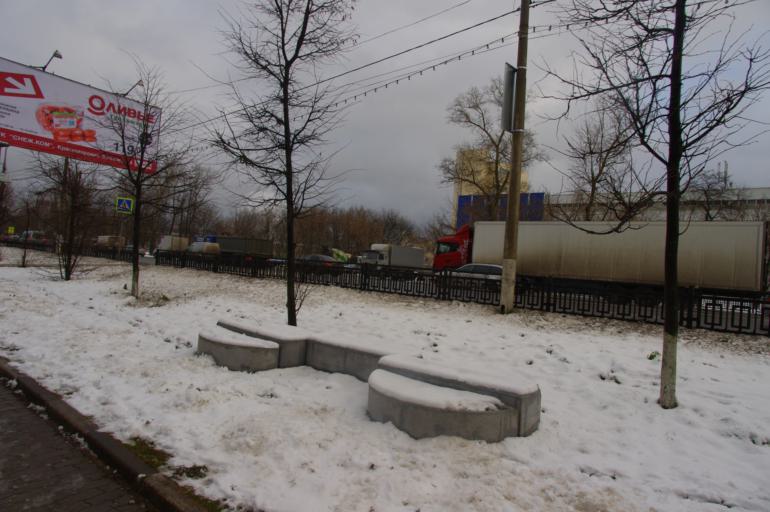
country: RU
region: Moskovskaya
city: Krasnogorsk
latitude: 55.8079
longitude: 37.3329
